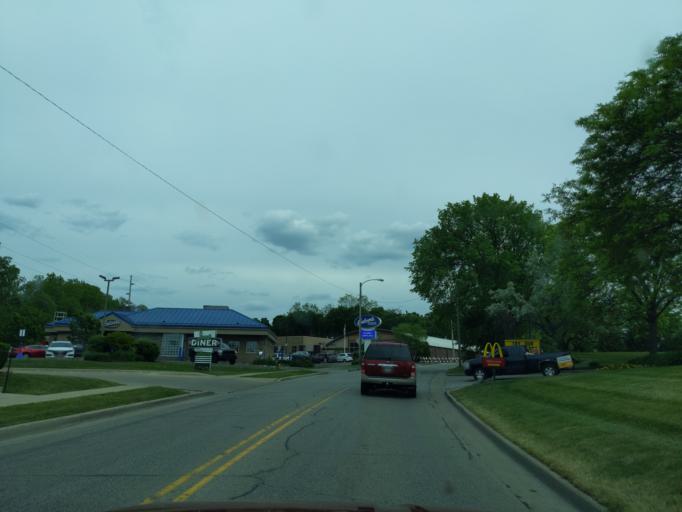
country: US
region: Wisconsin
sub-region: Walworth County
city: Lake Geneva
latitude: 42.5907
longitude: -88.4294
